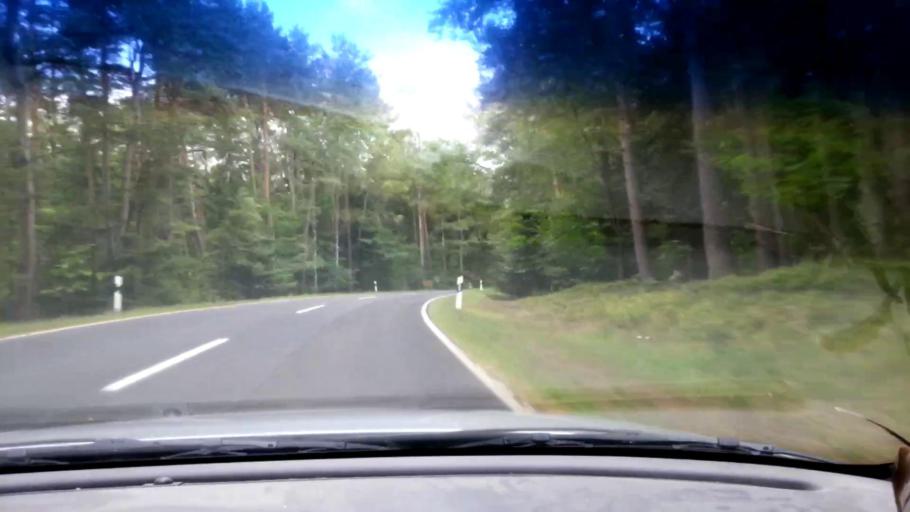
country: DE
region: Bavaria
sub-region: Upper Palatinate
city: Waldsassen
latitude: 50.0272
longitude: 12.3078
